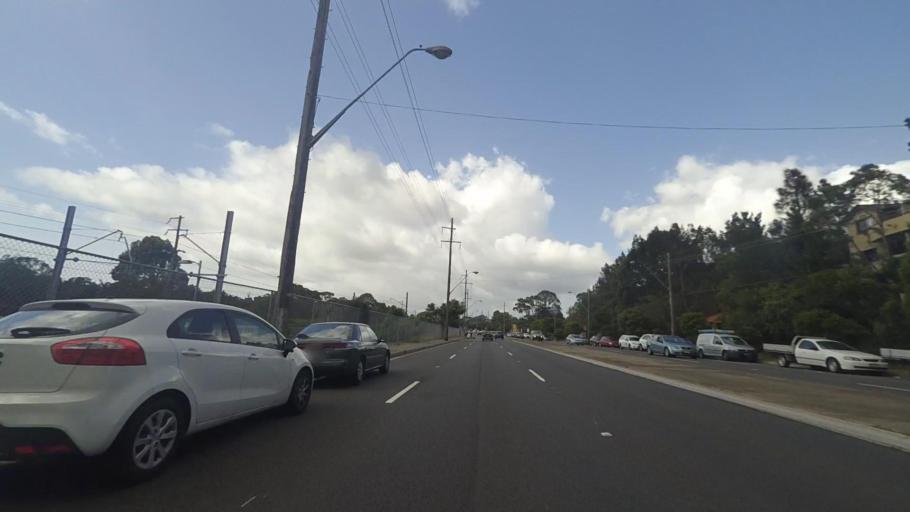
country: AU
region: New South Wales
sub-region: Sutherland Shire
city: Engadine
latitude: -34.0684
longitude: 151.0140
